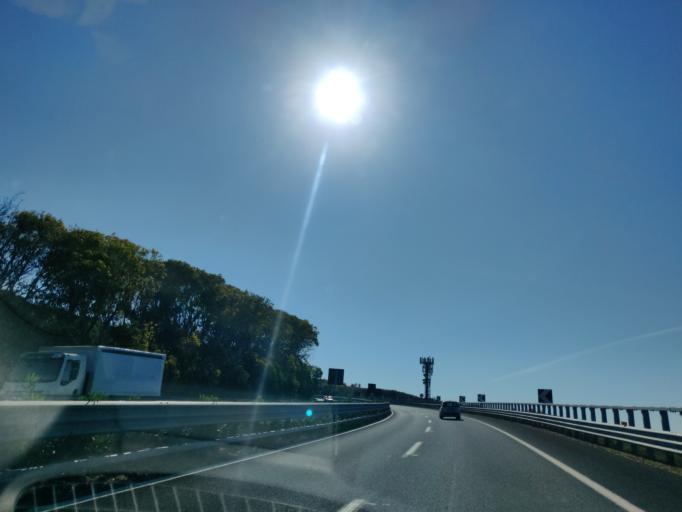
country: IT
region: Latium
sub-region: Citta metropolitana di Roma Capitale
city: Santa Marinella
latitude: 42.0401
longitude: 11.8479
